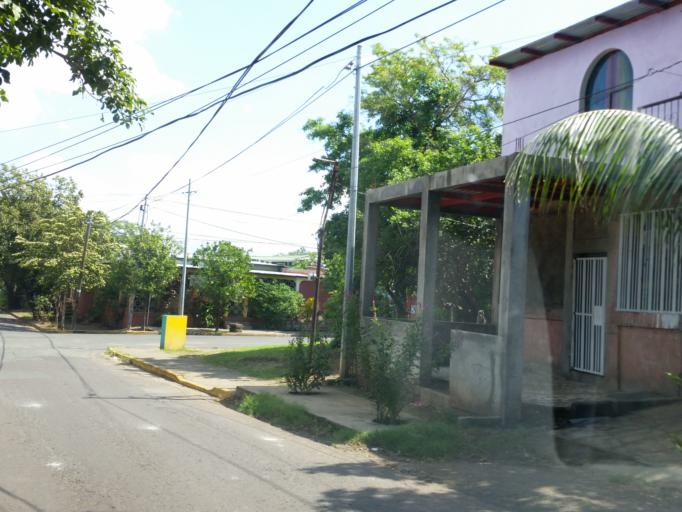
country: NI
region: Managua
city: Managua
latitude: 12.1199
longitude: -86.2720
